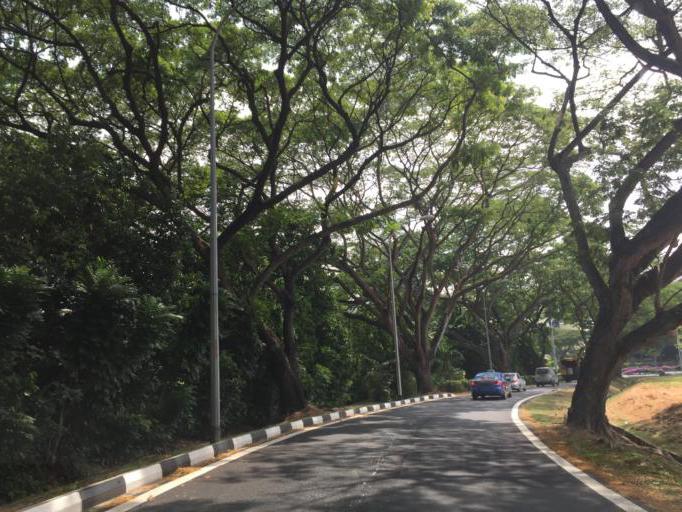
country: SG
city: Singapore
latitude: 1.3395
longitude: 103.9466
